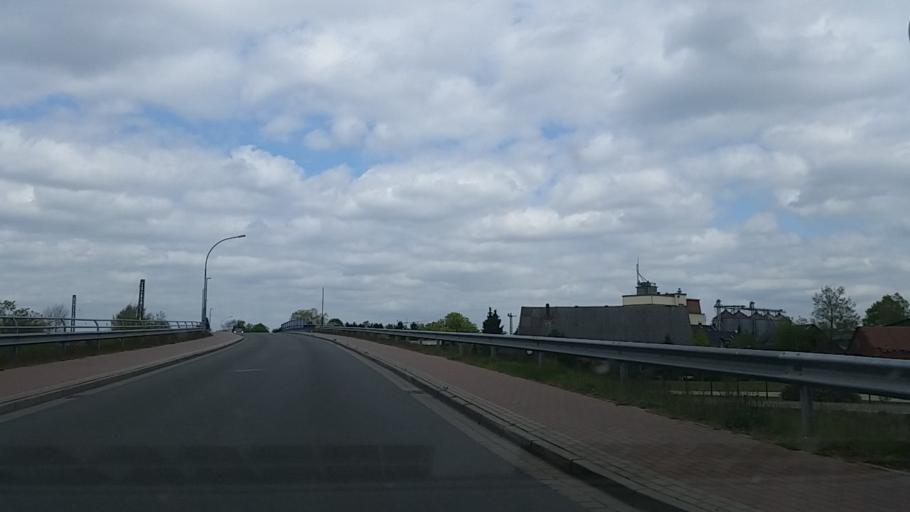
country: DE
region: Lower Saxony
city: Tostedt
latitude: 53.2733
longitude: 9.7377
